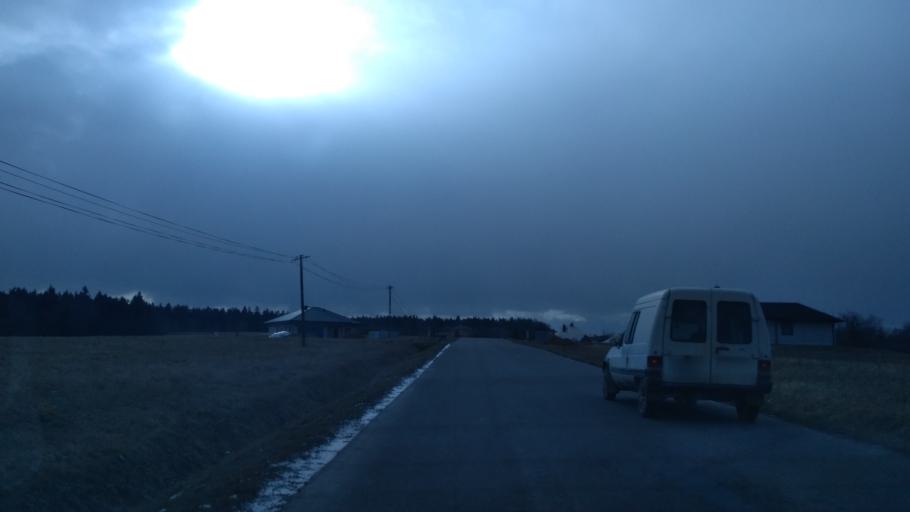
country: PL
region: Subcarpathian Voivodeship
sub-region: Powiat rzeszowski
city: Blazowa
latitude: 49.8446
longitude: 22.0886
